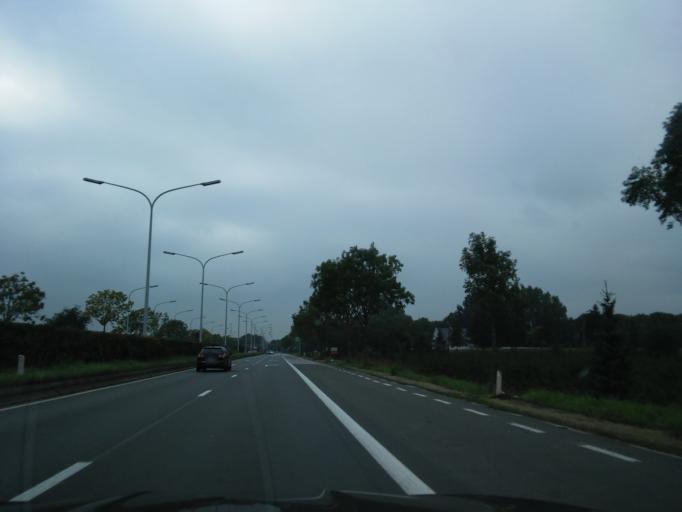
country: BE
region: Flanders
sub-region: Provincie Oost-Vlaanderen
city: Zele
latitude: 51.0859
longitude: 4.0299
